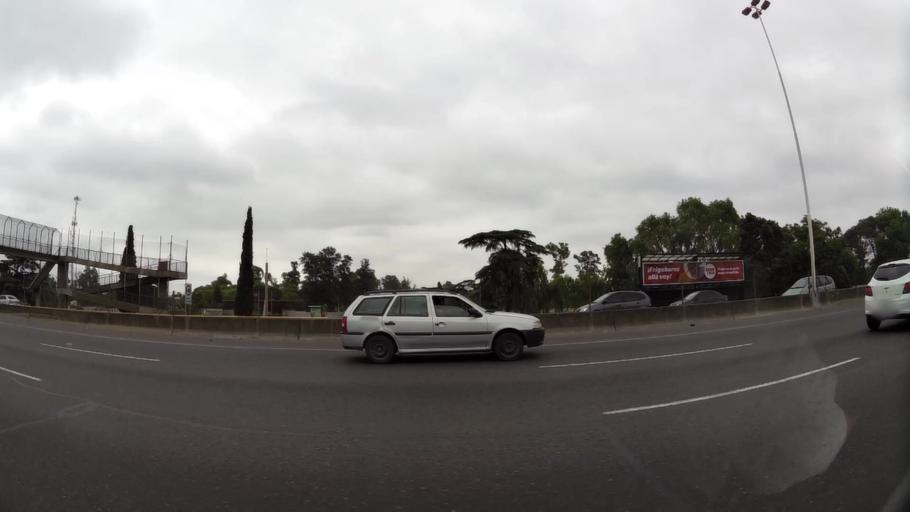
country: AR
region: Buenos Aires
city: San Justo
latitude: -34.7442
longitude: -58.5212
